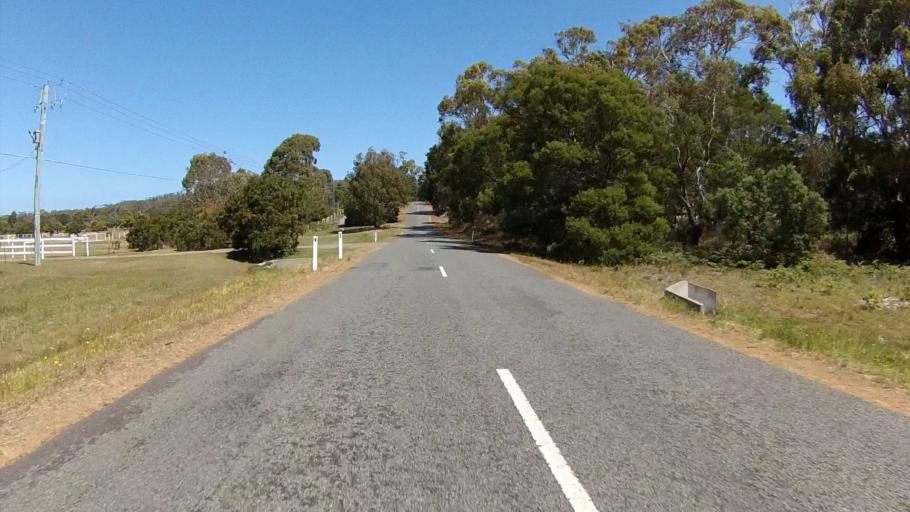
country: AU
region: Tasmania
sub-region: Clarence
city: Sandford
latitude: -42.9903
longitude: 147.4791
